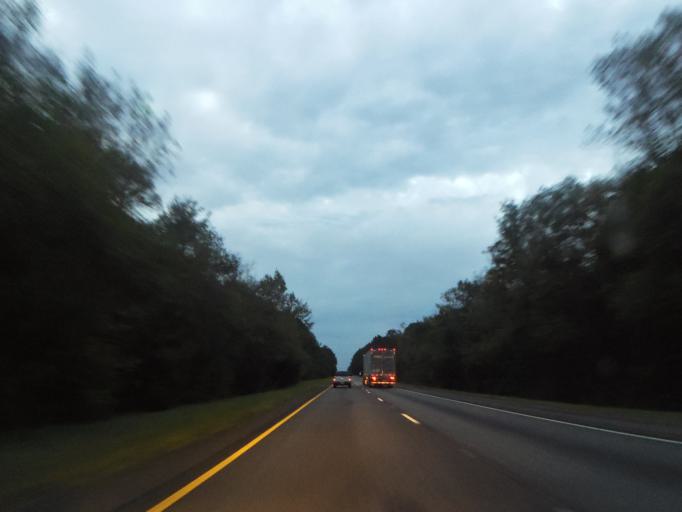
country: US
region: Alabama
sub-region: Etowah County
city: Whitesboro
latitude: 34.1652
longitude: -85.9731
